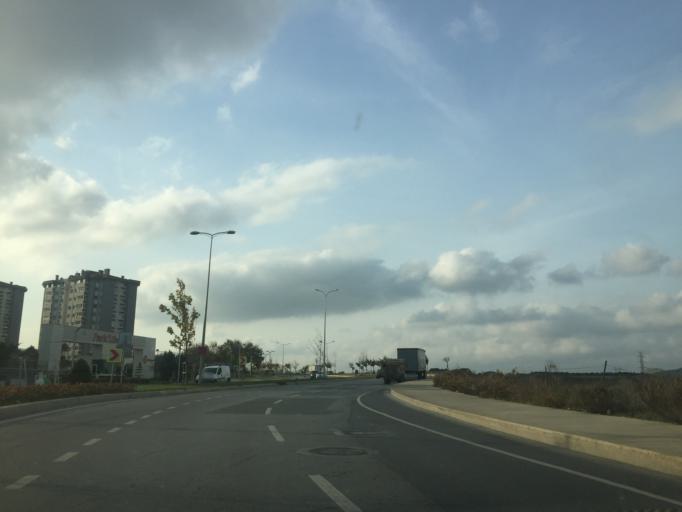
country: TR
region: Istanbul
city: Sultanbeyli
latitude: 40.9398
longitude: 29.3176
